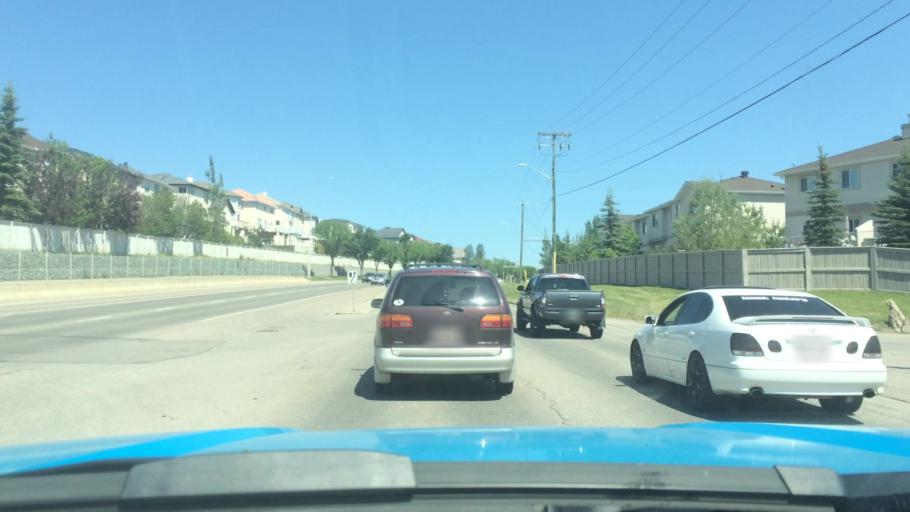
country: CA
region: Alberta
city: Calgary
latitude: 51.1459
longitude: -114.0840
